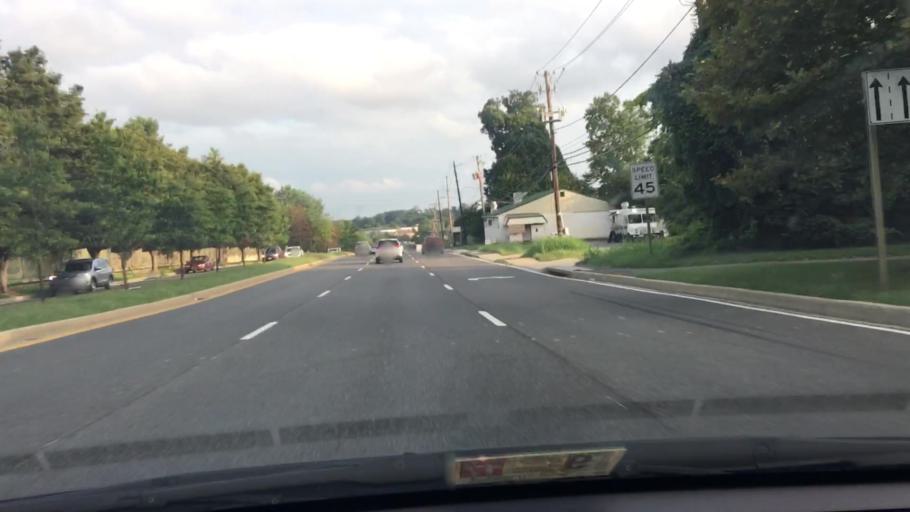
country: US
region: Maryland
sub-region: Montgomery County
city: Germantown
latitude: 39.1887
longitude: -77.2411
